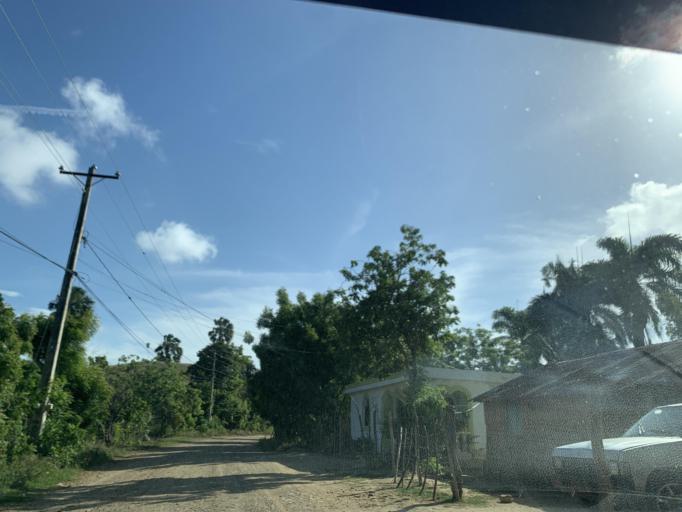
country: DO
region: Puerto Plata
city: Luperon
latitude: 19.8896
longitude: -70.8861
